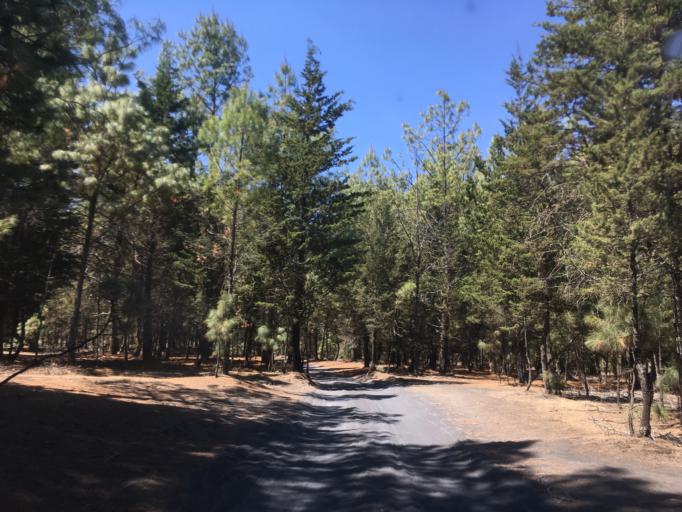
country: MX
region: Michoacan
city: Angahuan
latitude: 19.4628
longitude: -102.2342
